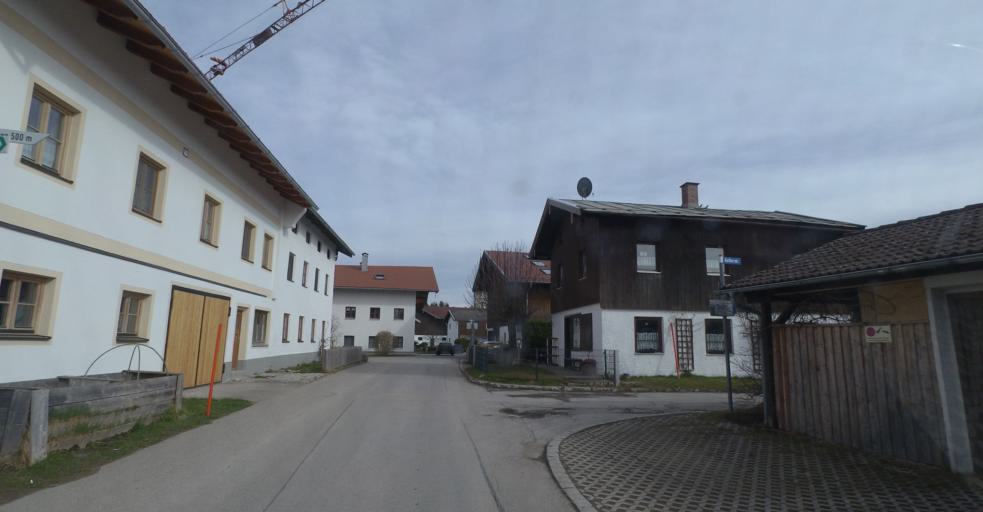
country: DE
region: Bavaria
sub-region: Upper Bavaria
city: Chieming
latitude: 47.9269
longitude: 12.5486
